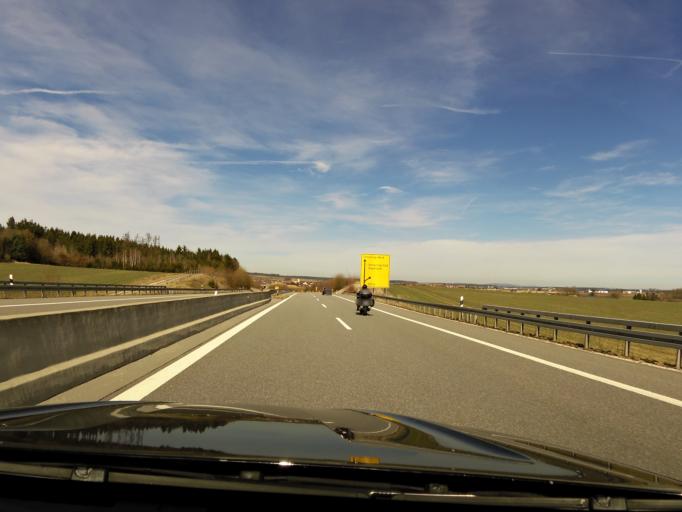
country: DE
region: Bavaria
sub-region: Upper Palatinate
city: Schierling
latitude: 48.8129
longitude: 12.1336
